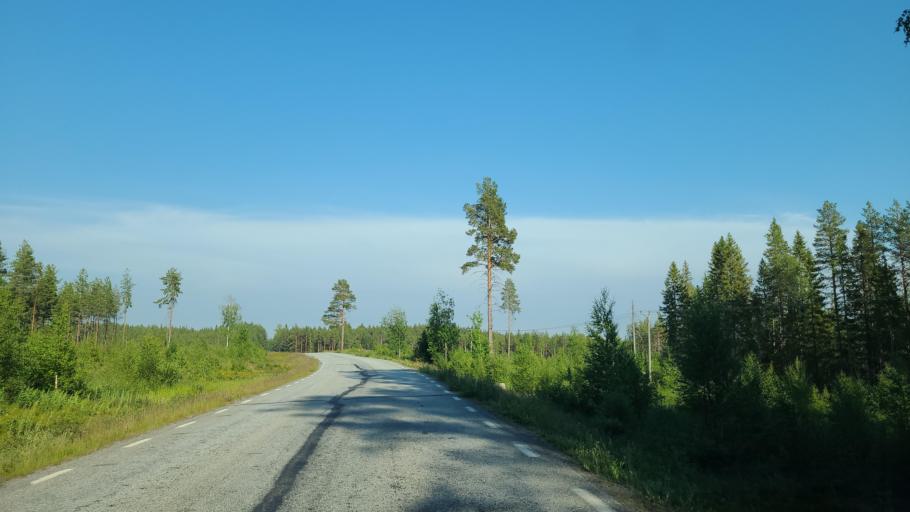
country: SE
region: Vaesterbotten
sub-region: Robertsfors Kommun
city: Robertsfors
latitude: 64.2799
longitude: 20.9922
